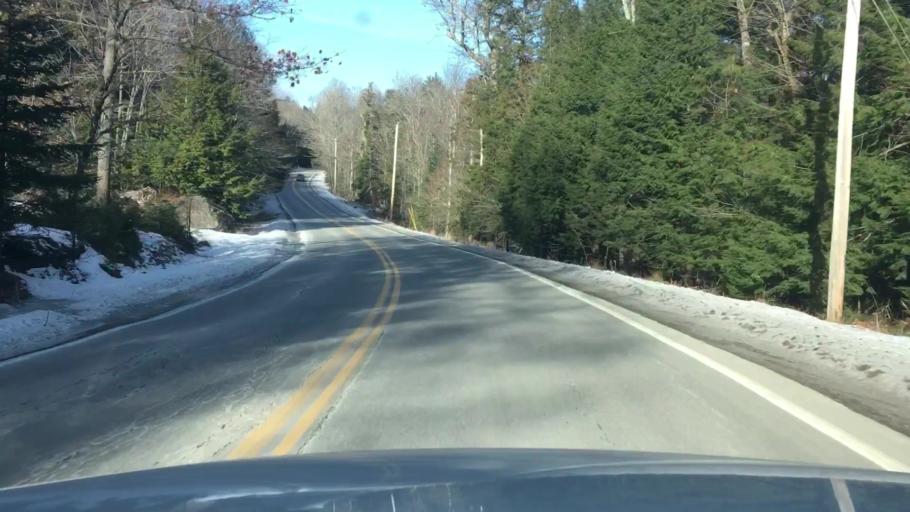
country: US
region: Maine
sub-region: Hancock County
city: Dedham
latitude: 44.6347
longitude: -68.6995
